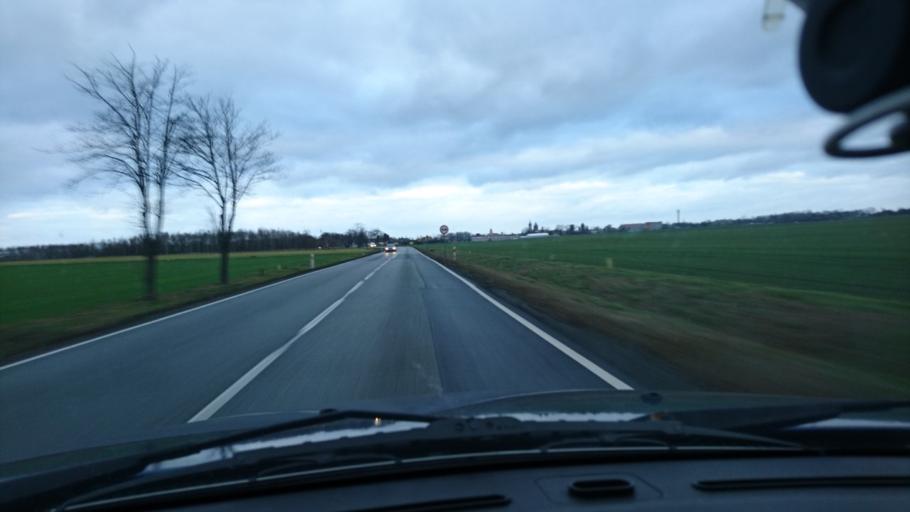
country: PL
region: Opole Voivodeship
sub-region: Powiat kluczborski
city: Byczyna
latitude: 51.1032
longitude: 18.2059
